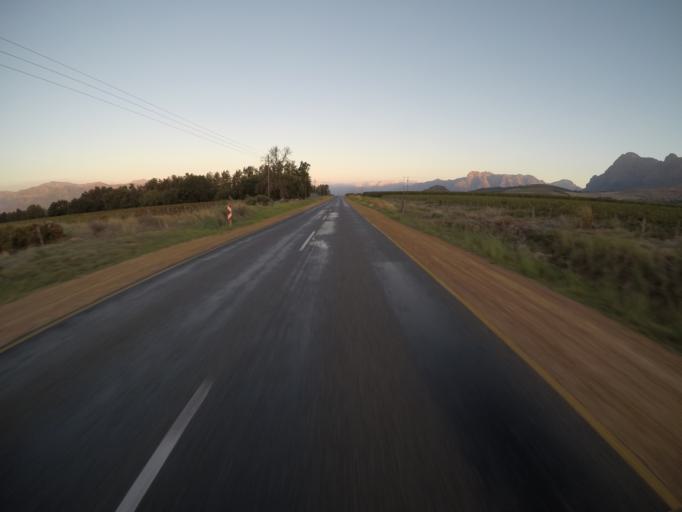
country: ZA
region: Western Cape
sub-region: Cape Winelands District Municipality
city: Paarl
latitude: -33.8168
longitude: 18.9194
